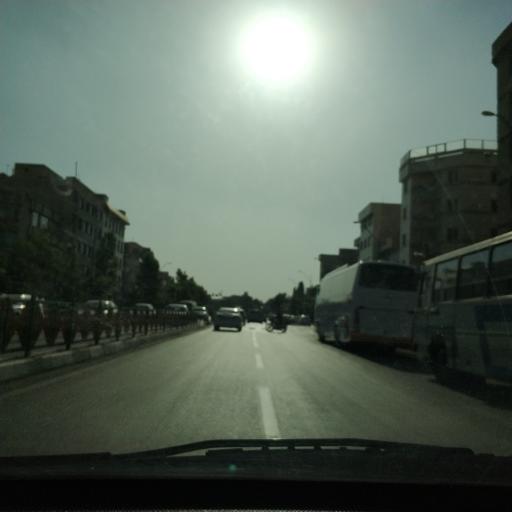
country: IR
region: Tehran
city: Tehran
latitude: 35.7216
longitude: 51.4792
